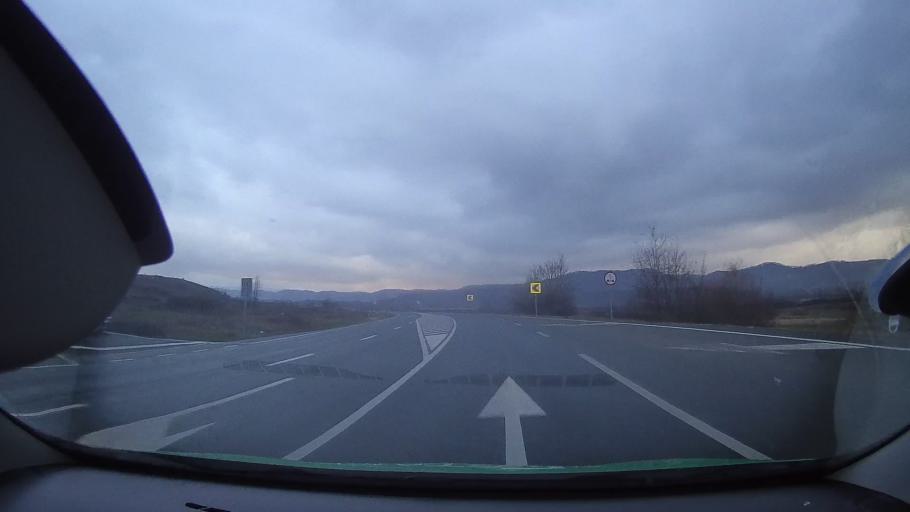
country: RO
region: Hunedoara
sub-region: Comuna Ribita
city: Ribita
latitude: 46.1655
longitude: 22.7514
